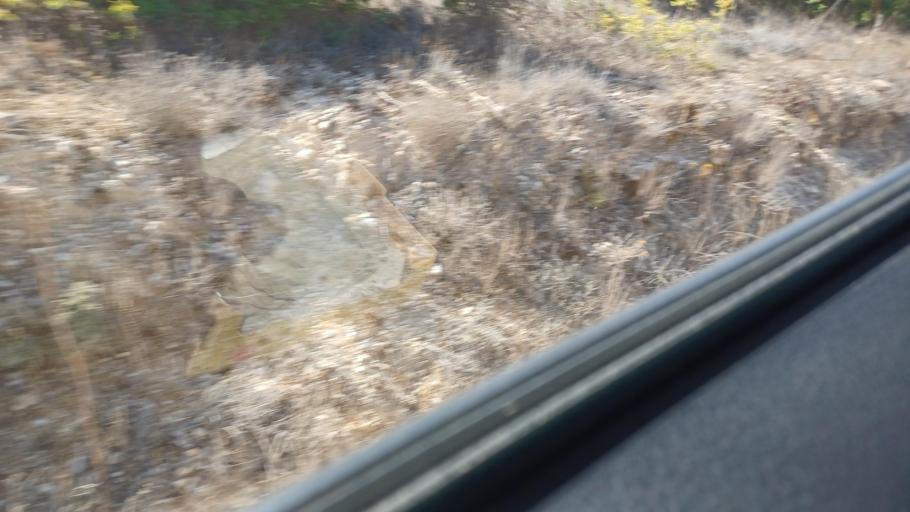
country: CY
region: Pafos
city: Tala
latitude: 34.8696
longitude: 32.4396
